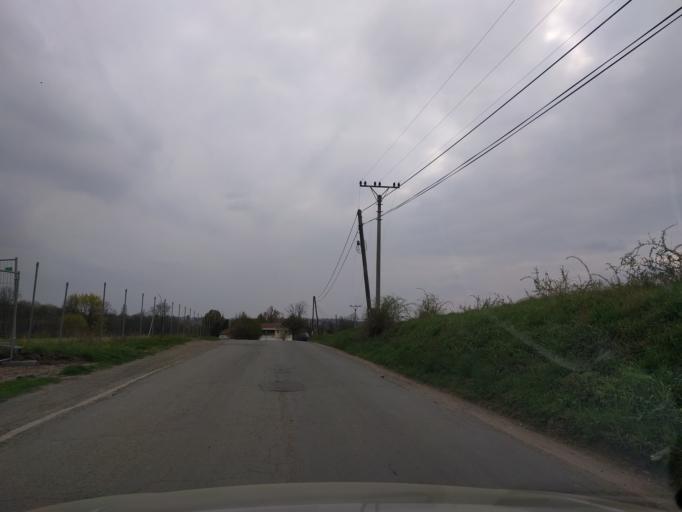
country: CZ
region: Central Bohemia
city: Cesky Brod
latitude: 50.0625
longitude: 14.8476
